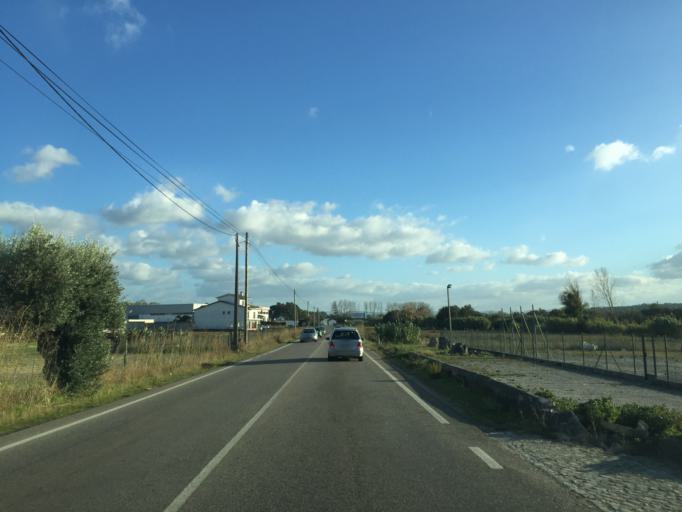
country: PT
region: Leiria
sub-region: Leiria
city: Amor
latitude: 39.8017
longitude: -8.8387
